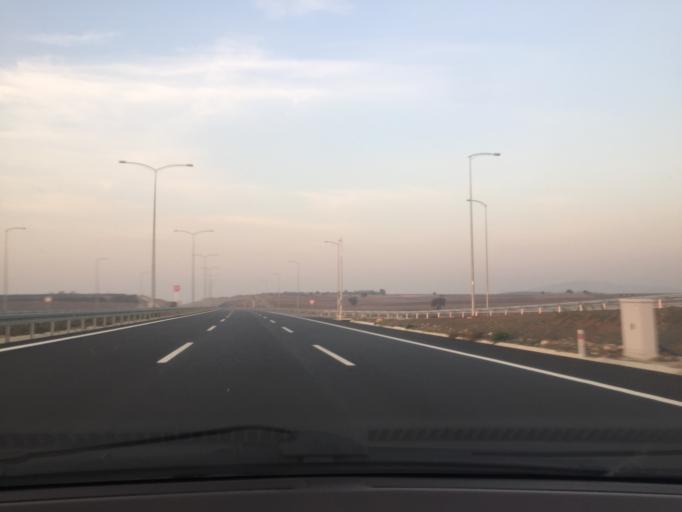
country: TR
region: Bursa
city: Karacabey
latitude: 40.2503
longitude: 28.4473
